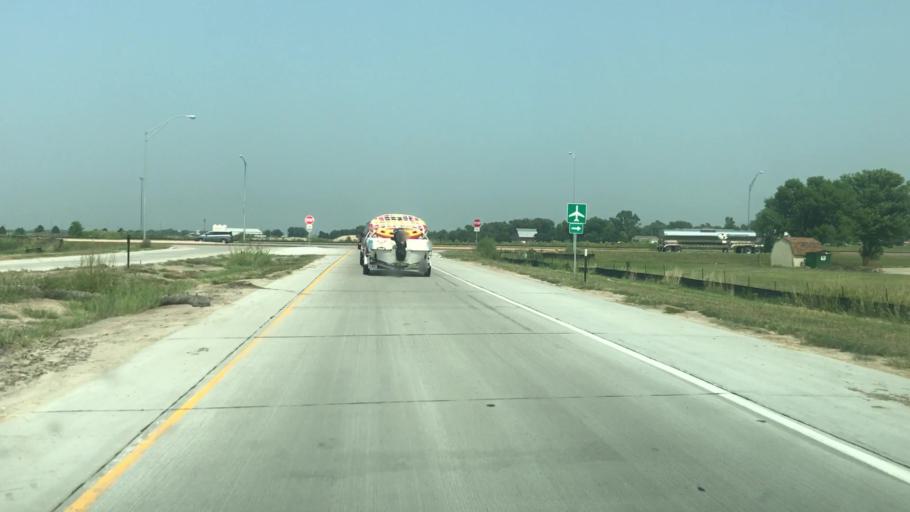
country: US
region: Nebraska
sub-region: Hall County
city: Grand Island
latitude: 40.9522
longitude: -98.3827
